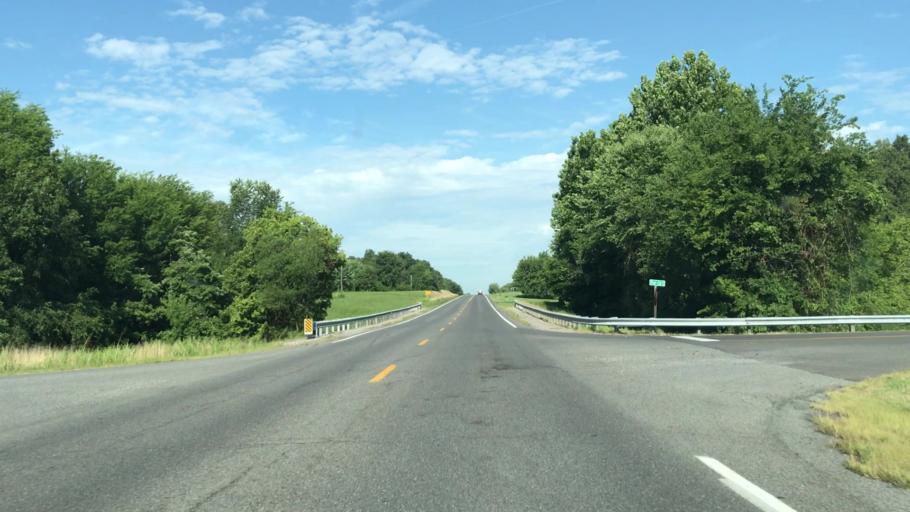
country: US
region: Kentucky
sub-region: Livingston County
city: Ledbetter
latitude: 37.0066
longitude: -88.4522
